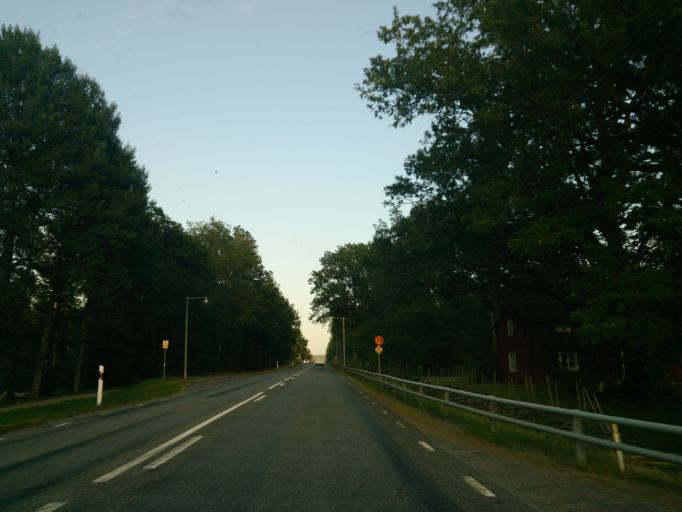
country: SE
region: Joenkoeping
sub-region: Varnamo Kommun
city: Bor
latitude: 57.1257
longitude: 14.1388
